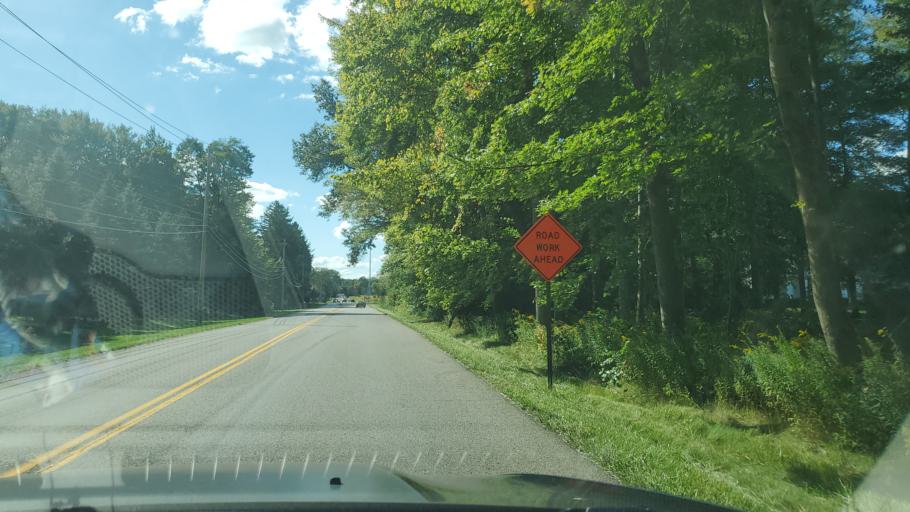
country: US
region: Ohio
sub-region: Mahoning County
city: Canfield
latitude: 41.0425
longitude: -80.7332
